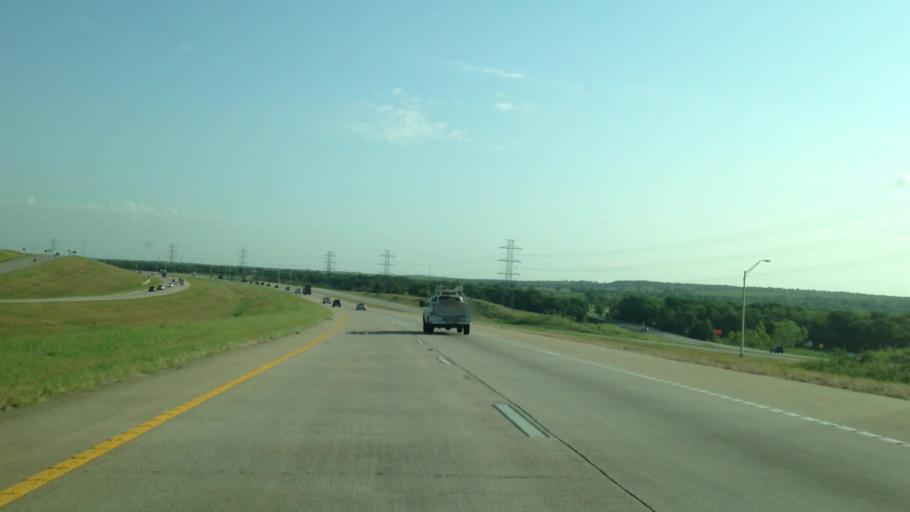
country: US
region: Texas
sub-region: Travis County
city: Hornsby Bend
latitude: 30.2940
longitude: -97.5712
